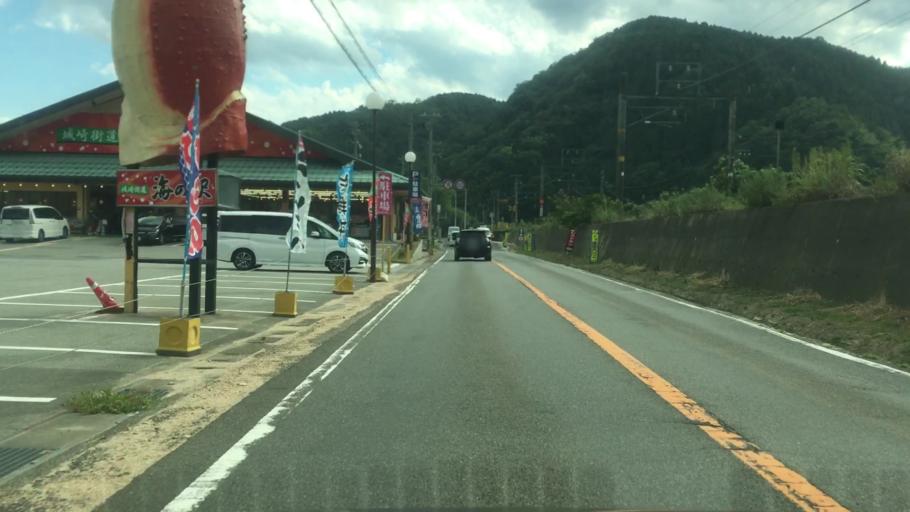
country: JP
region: Hyogo
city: Toyooka
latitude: 35.5937
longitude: 134.8007
